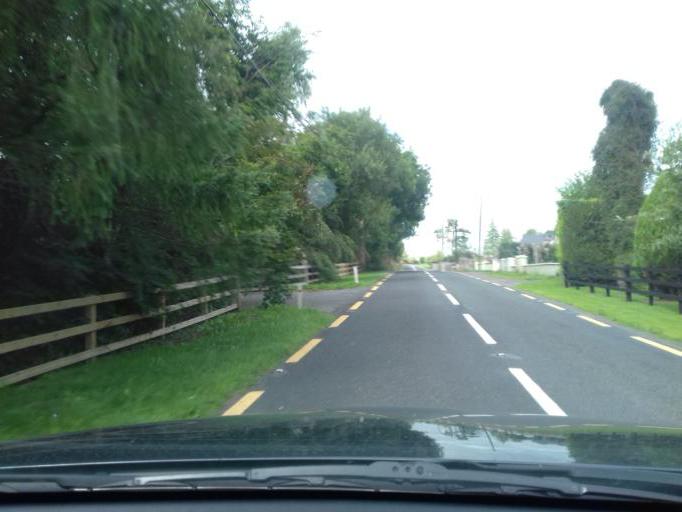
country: IE
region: Leinster
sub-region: County Carlow
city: Tullow
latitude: 52.8519
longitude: -6.7107
